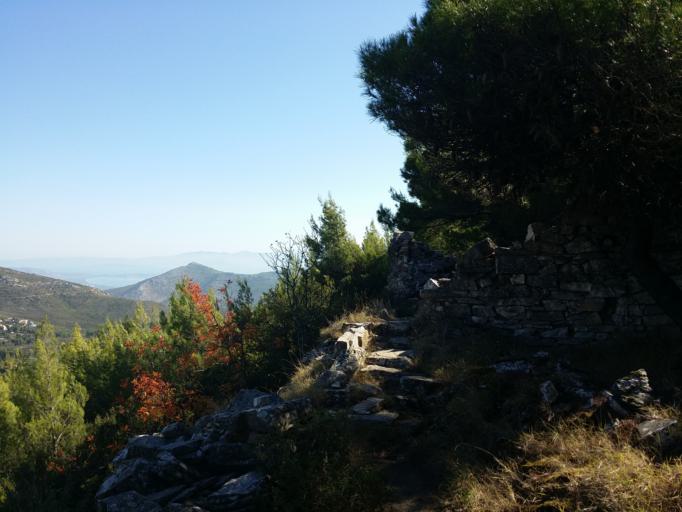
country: GR
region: Attica
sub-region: Nomarchia Anatolikis Attikis
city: Dionysos
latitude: 38.0921
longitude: 23.8754
